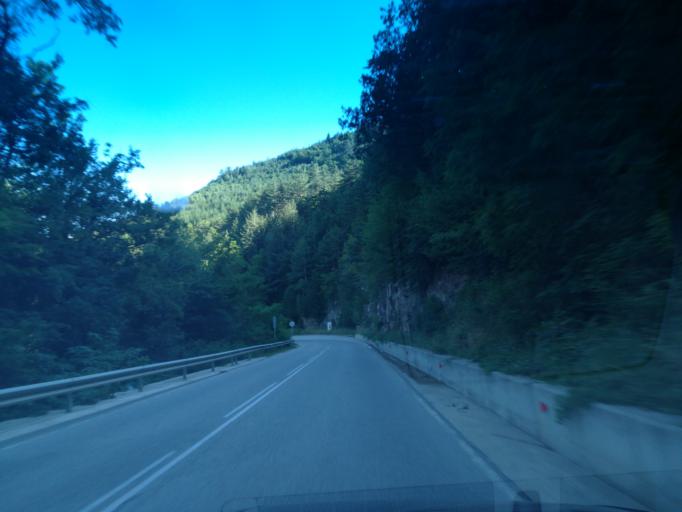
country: BG
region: Smolyan
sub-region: Obshtina Chepelare
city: Chepelare
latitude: 41.8372
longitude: 24.6797
